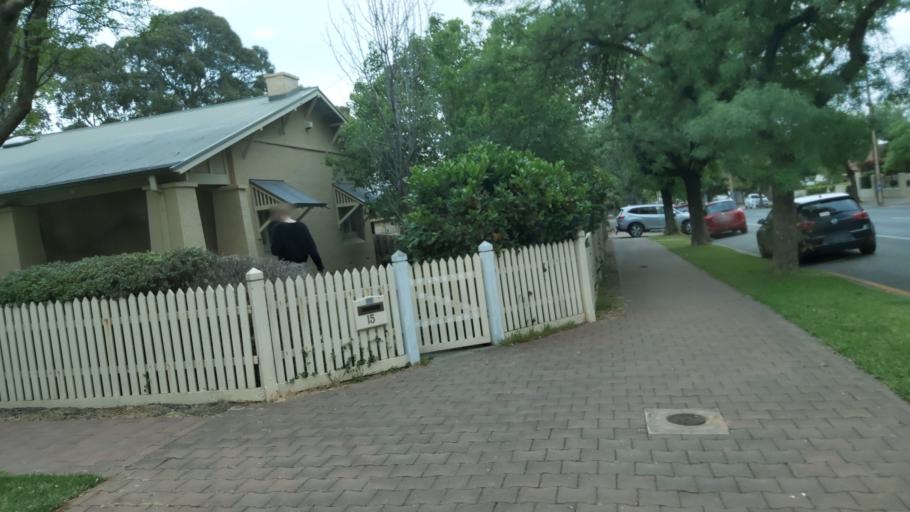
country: AU
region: South Australia
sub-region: Burnside
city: Glenunga
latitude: -34.9564
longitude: 138.6360
